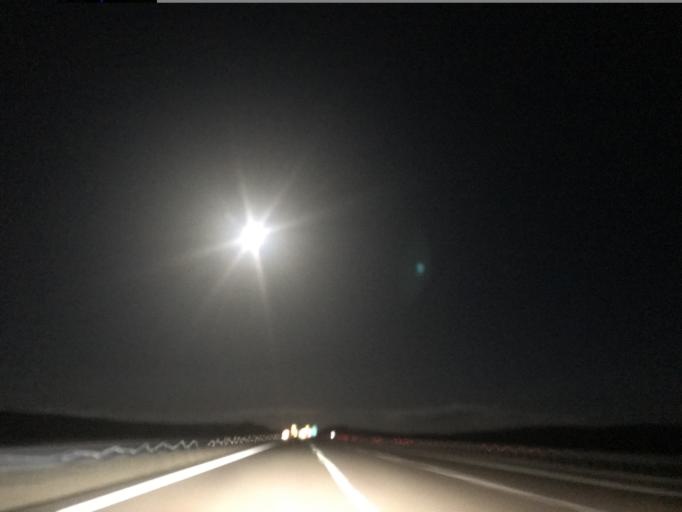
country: TR
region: Nigde
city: Ulukisla
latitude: 37.6363
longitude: 34.5032
